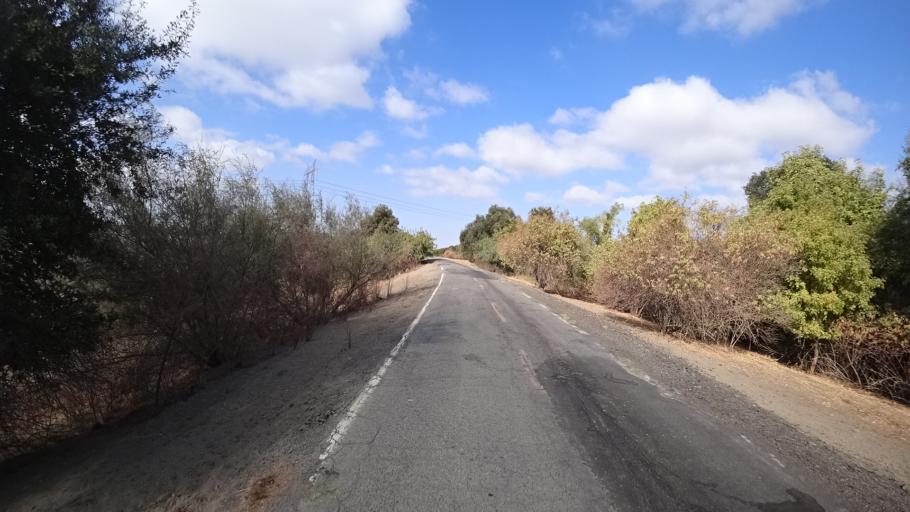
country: US
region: California
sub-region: Yolo County
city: Woodland
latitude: 38.7625
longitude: -121.6812
